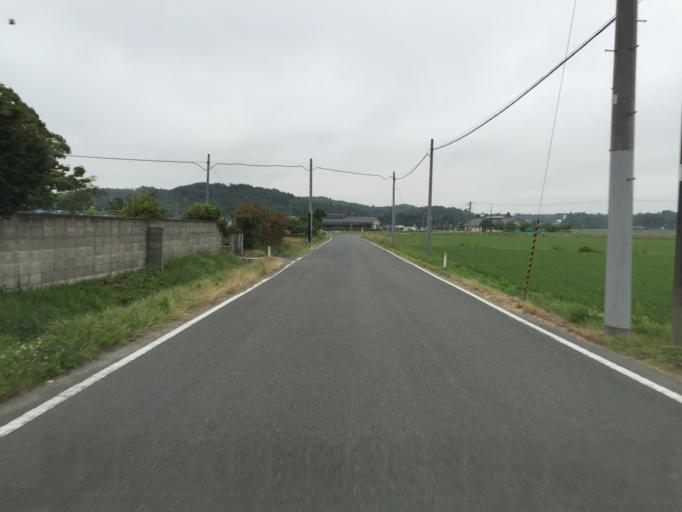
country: JP
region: Miyagi
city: Marumori
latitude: 37.7626
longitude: 140.9448
